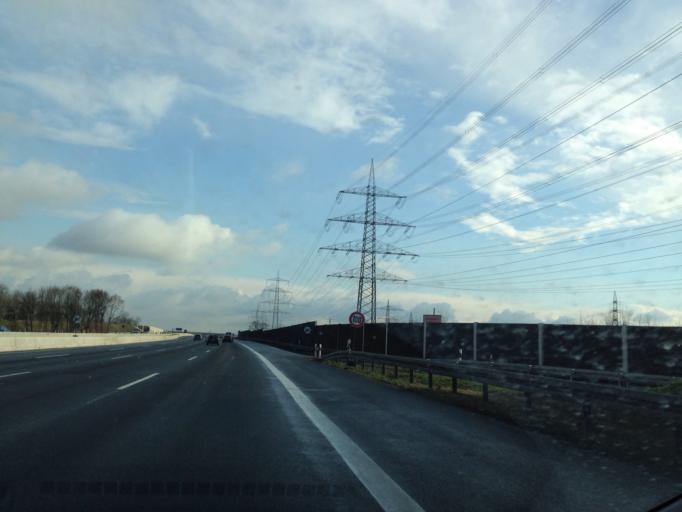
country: DE
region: North Rhine-Westphalia
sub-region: Regierungsbezirk Dusseldorf
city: Kaarst
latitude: 51.2195
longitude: 6.6411
